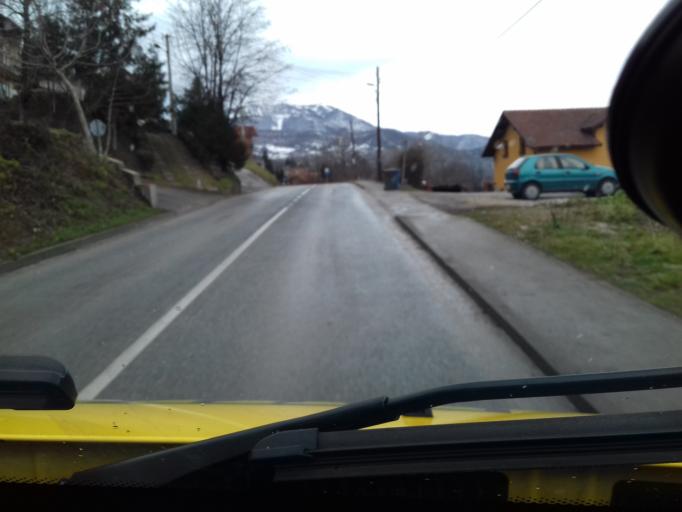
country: BA
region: Federation of Bosnia and Herzegovina
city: Zenica
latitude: 44.2116
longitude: 17.8929
